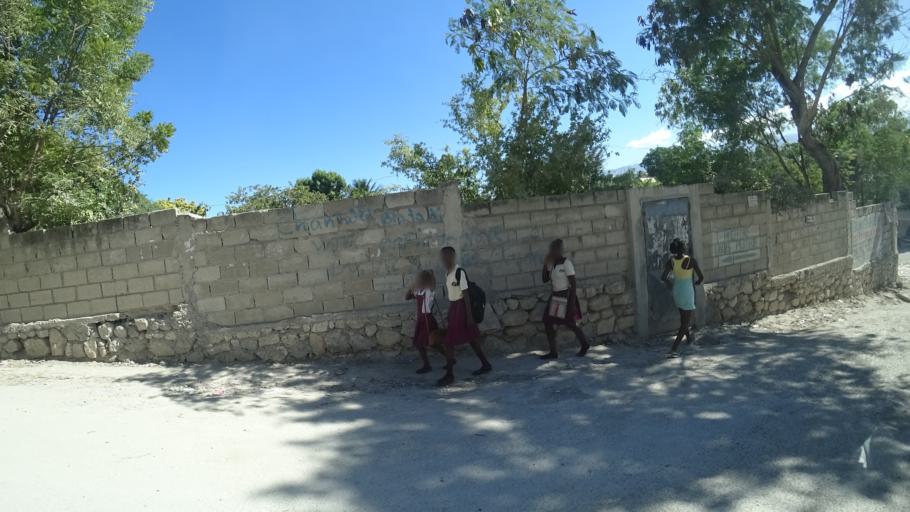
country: HT
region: Ouest
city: Delmas 73
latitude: 18.5608
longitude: -72.2863
